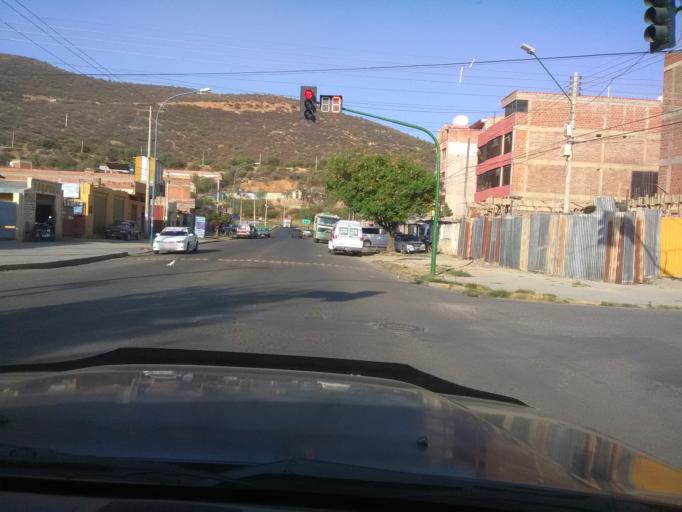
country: BO
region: Cochabamba
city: Cochabamba
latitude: -17.3985
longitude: -66.1377
